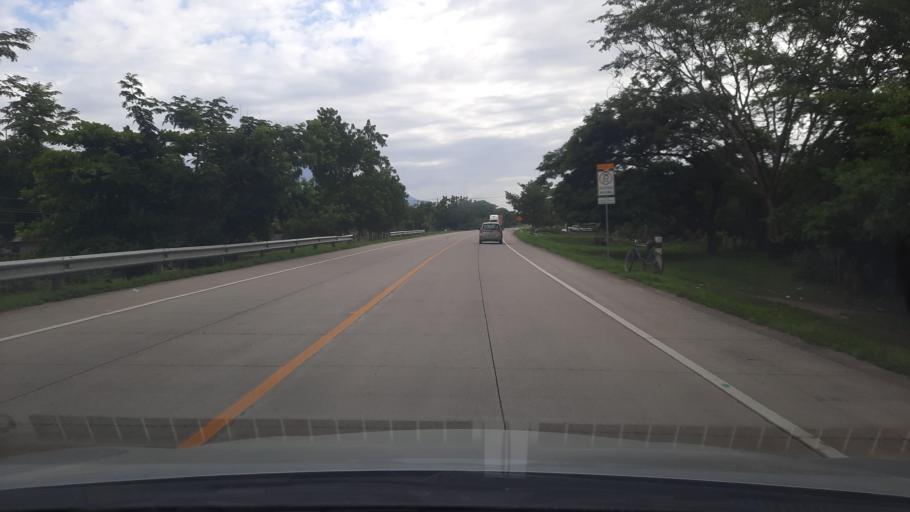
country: NI
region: Chinandega
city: Somotillo
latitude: 12.8407
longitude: -86.8830
